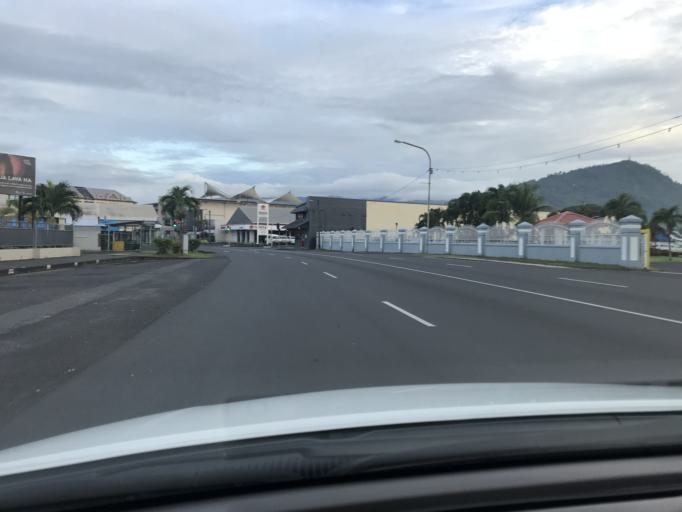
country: WS
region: Tuamasaga
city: Apia
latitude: -13.8289
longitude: -171.7720
